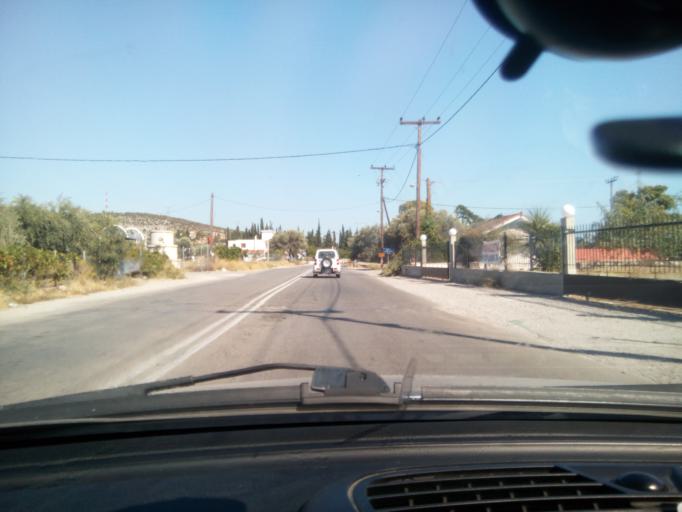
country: GR
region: Central Greece
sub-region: Nomos Evvoias
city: Malakonta
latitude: 38.4065
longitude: 23.7393
